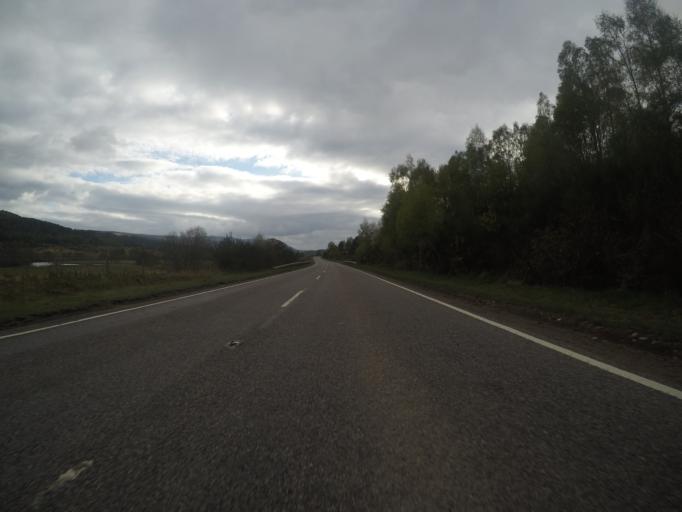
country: GB
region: Scotland
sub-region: Highland
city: Spean Bridge
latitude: 57.1922
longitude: -4.7599
